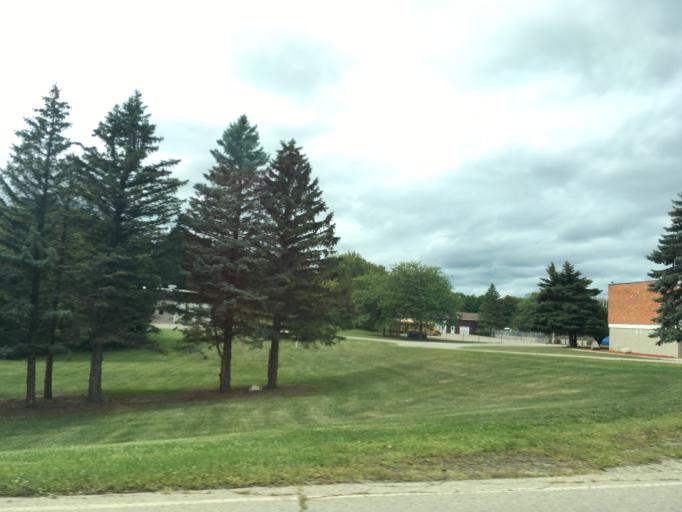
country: US
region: Michigan
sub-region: Lapeer County
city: Barnes Lake-Millers Lake
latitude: 43.3311
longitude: -83.3524
